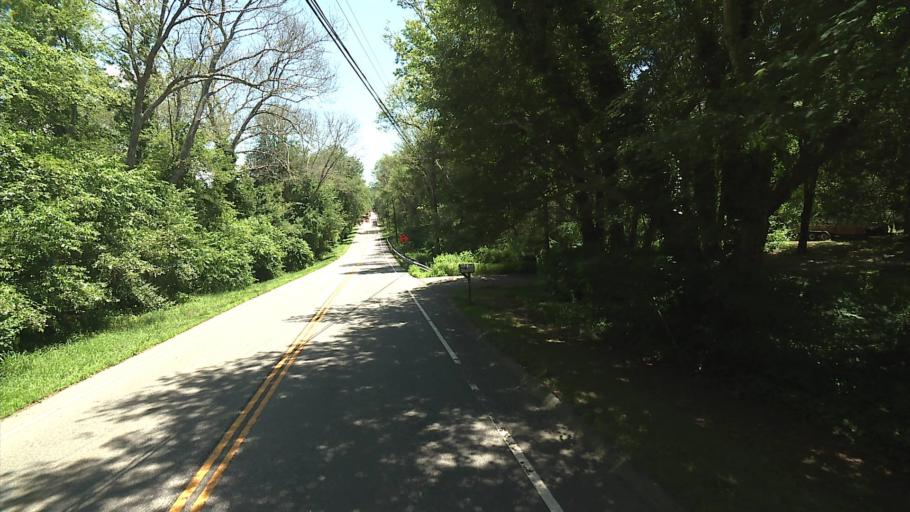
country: US
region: Connecticut
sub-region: New London County
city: Pawcatuck
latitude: 41.3826
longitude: -71.8786
